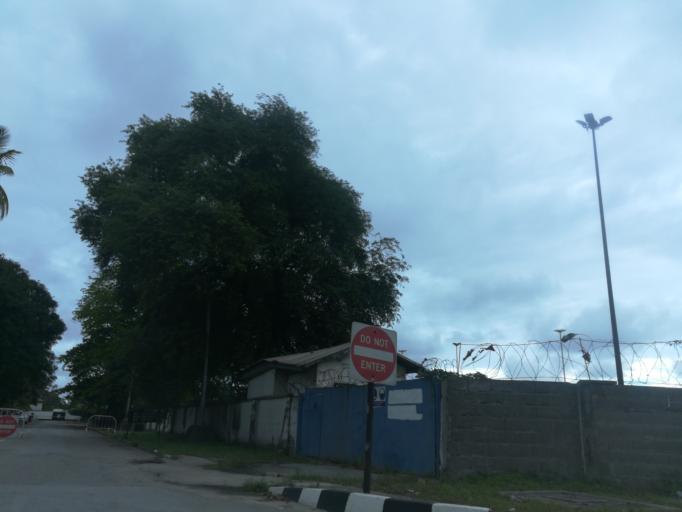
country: NG
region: Lagos
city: Lagos
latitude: 6.4457
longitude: 3.3978
